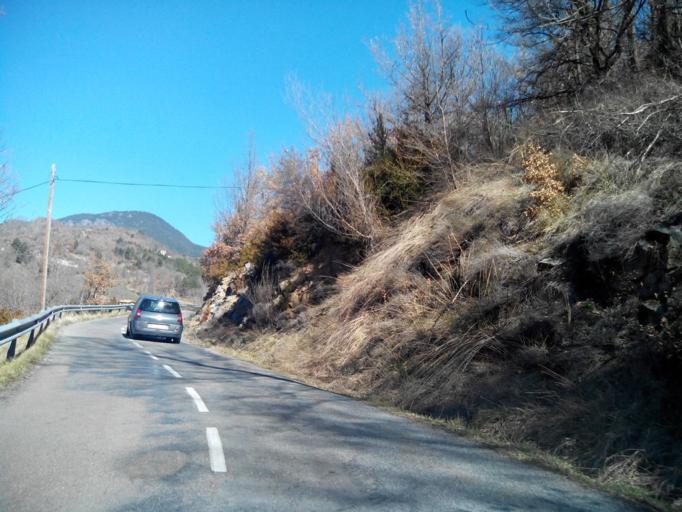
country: ES
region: Catalonia
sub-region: Provincia de Lleida
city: Lles de Cerdanya
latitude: 42.3646
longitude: 1.6853
